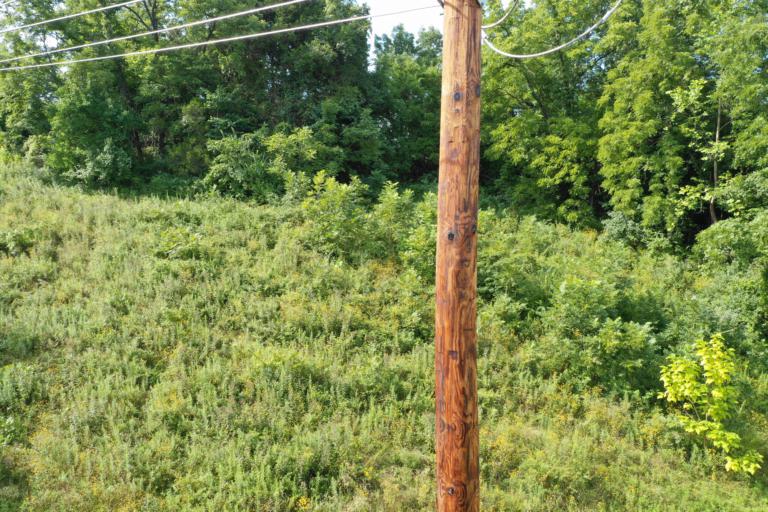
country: US
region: Missouri
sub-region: Callaway County
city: Holts Summit
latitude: 38.5330
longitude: -92.0451
